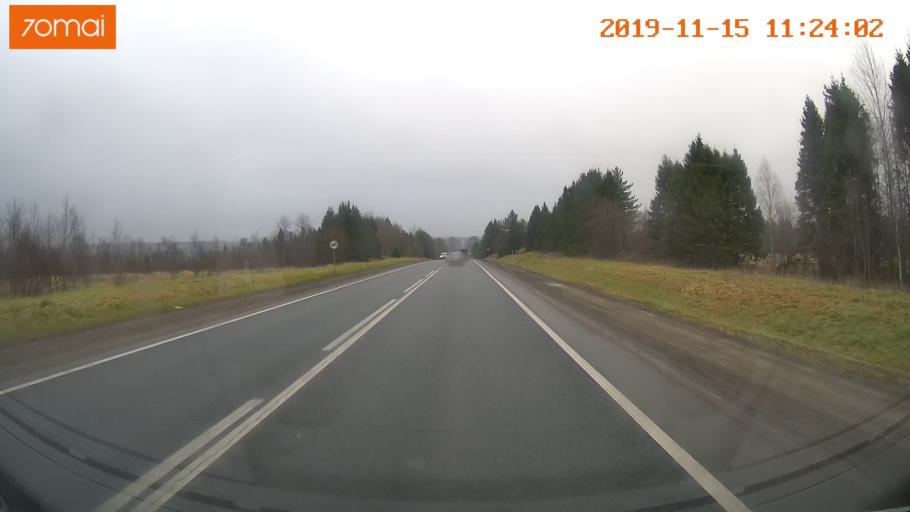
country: RU
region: Vologda
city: Molochnoye
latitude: 59.1550
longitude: 39.3963
